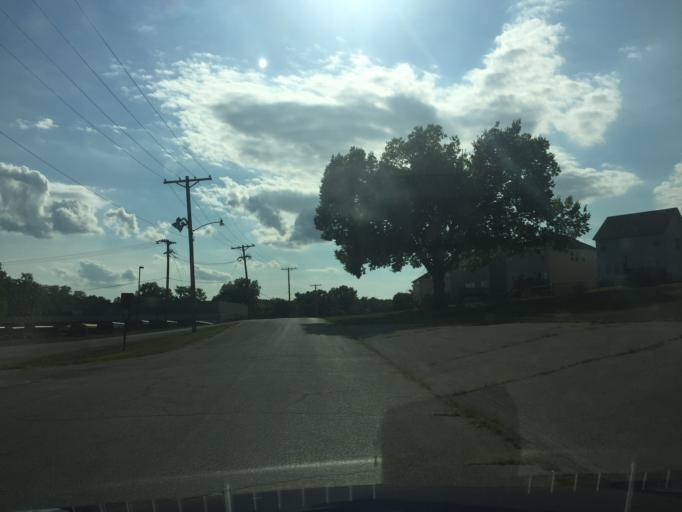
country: US
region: Kansas
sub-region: Leavenworth County
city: Leavenworth
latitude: 39.3367
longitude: -94.9177
